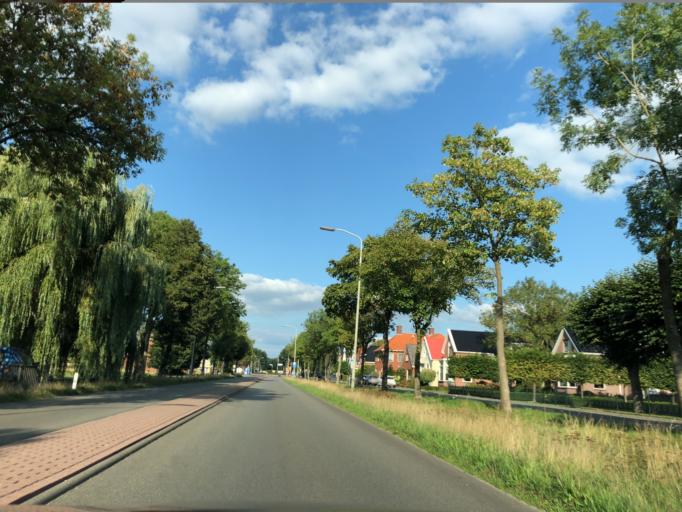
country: NL
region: Groningen
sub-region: Gemeente Stadskanaal
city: Stadskanaal
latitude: 52.9781
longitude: 6.9614
